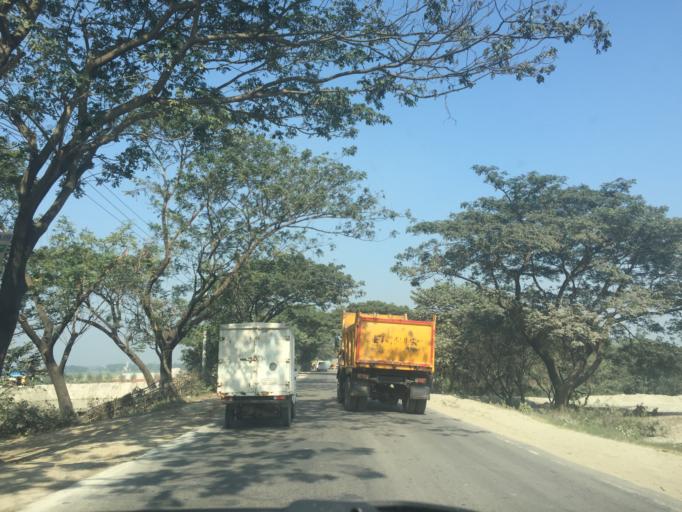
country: BD
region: Dhaka
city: Tungi
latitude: 23.8340
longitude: 90.3402
